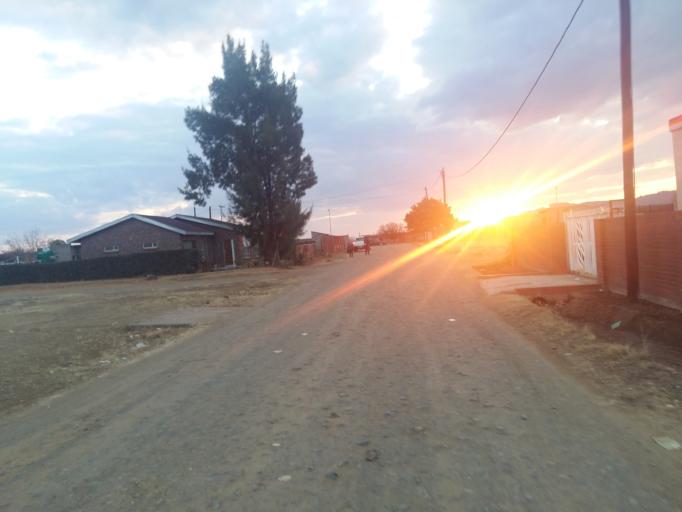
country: LS
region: Maseru
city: Maseru
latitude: -29.3826
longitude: 27.5308
